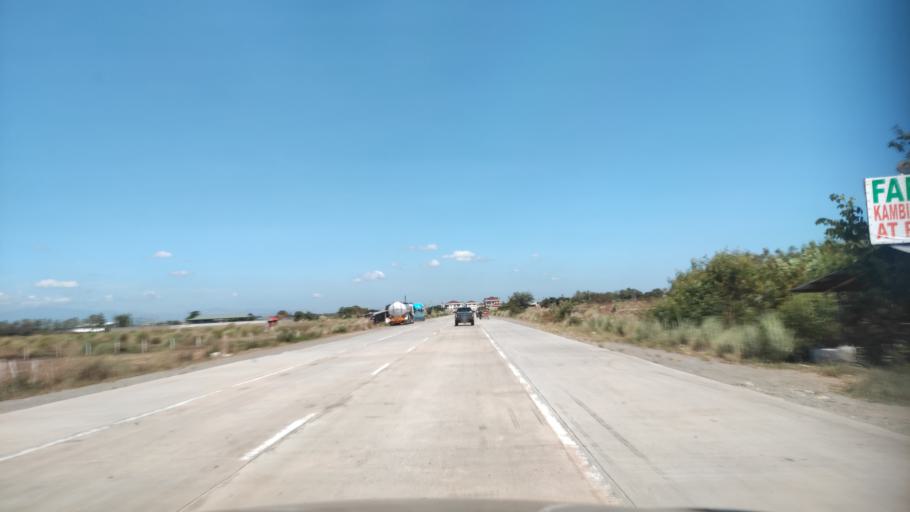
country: PH
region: Central Luzon
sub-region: Province of Tarlac
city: Salcedo
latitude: 15.8702
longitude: 120.6090
